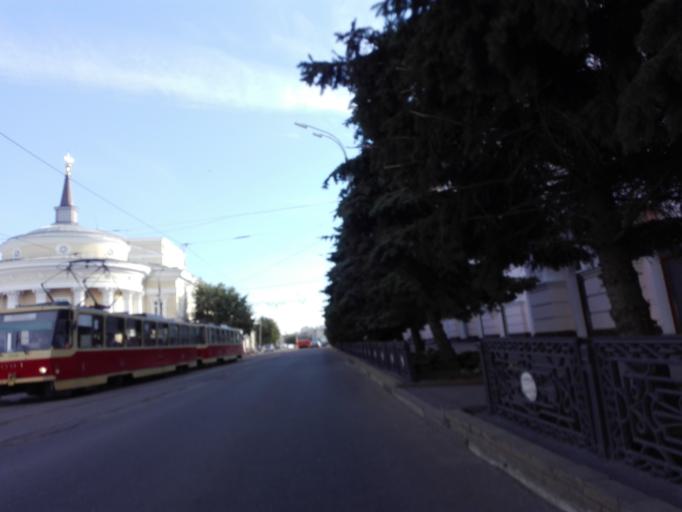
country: RU
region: Orjol
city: Orel
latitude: 52.9639
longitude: 36.0682
